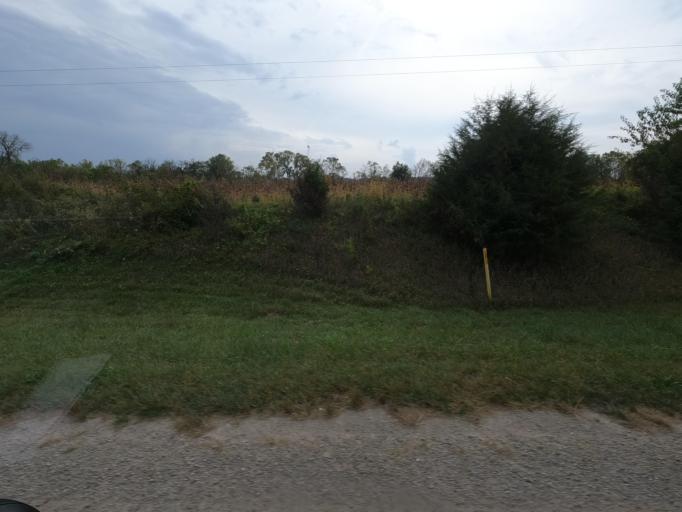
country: US
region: Iowa
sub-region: Van Buren County
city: Keosauqua
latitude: 40.8672
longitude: -92.1461
